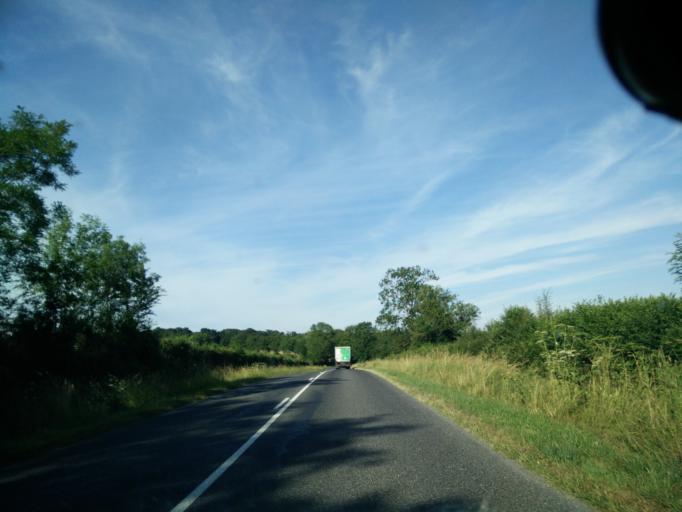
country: FR
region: Auvergne
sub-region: Departement de l'Allier
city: Souvigny
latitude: 46.5454
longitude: 3.2263
